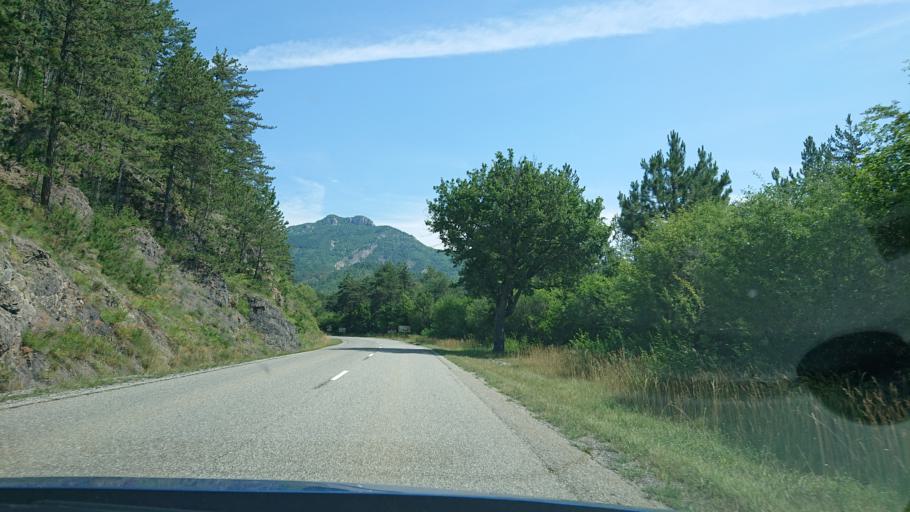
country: FR
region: Provence-Alpes-Cote d'Azur
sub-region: Departement des Alpes-de-Haute-Provence
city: Sisteron
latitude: 44.3059
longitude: 6.0345
